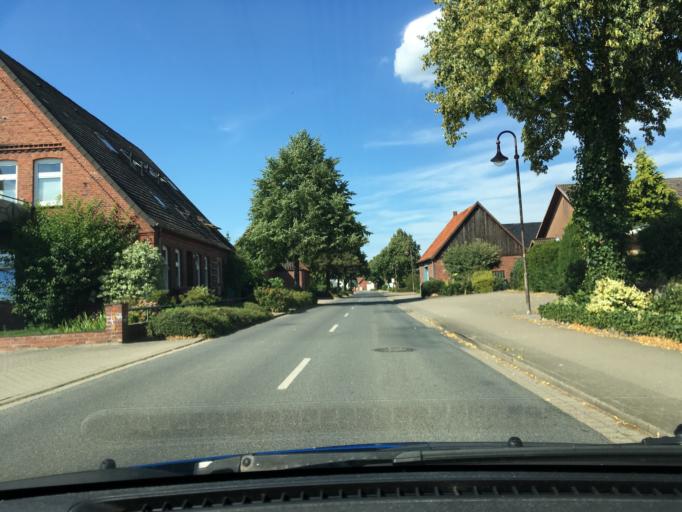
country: DE
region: Lower Saxony
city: Bardowick
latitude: 53.2994
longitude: 10.3863
